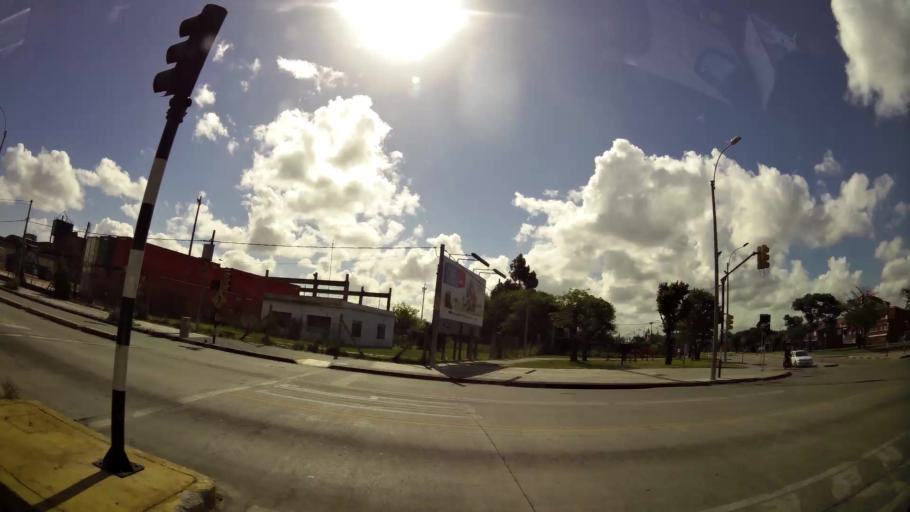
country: UY
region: Canelones
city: La Paz
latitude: -34.8277
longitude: -56.2200
